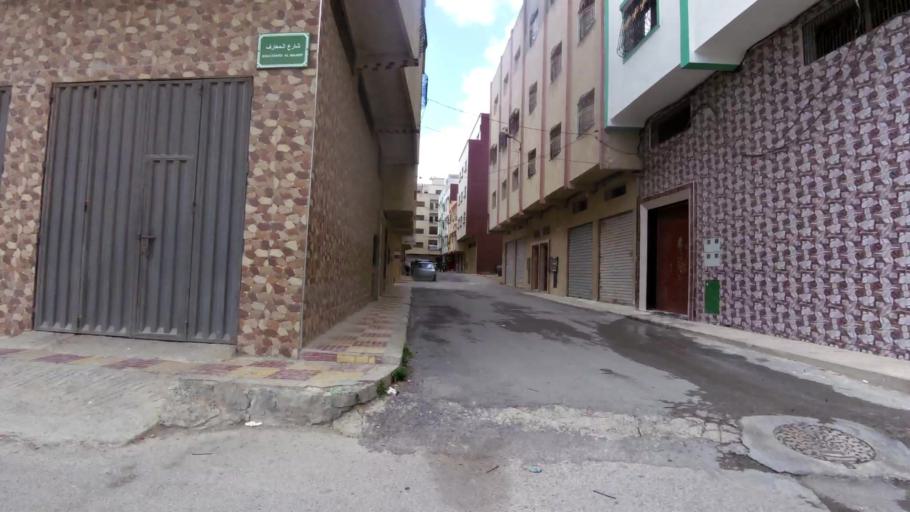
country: MA
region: Tanger-Tetouan
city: Tetouan
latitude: 35.5883
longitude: -5.3441
